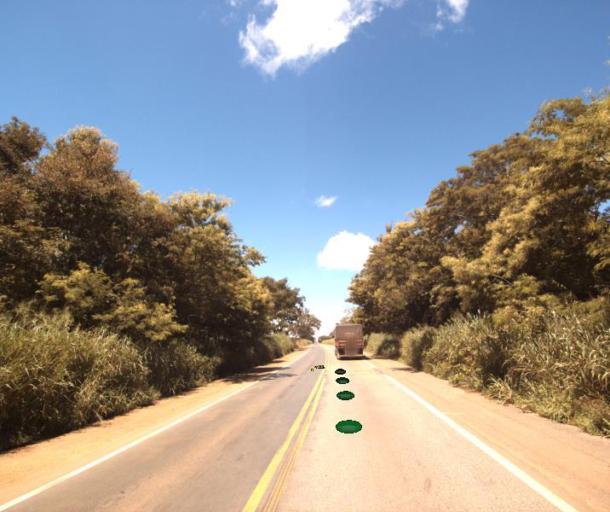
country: BR
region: Goias
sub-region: Anapolis
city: Anapolis
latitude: -16.1378
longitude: -49.0480
